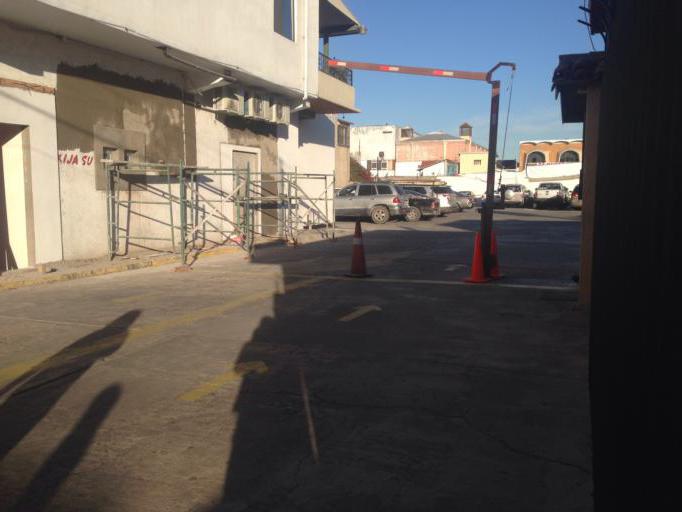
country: MX
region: Baja California
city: Tijuana
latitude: 32.5303
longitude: -117.0379
